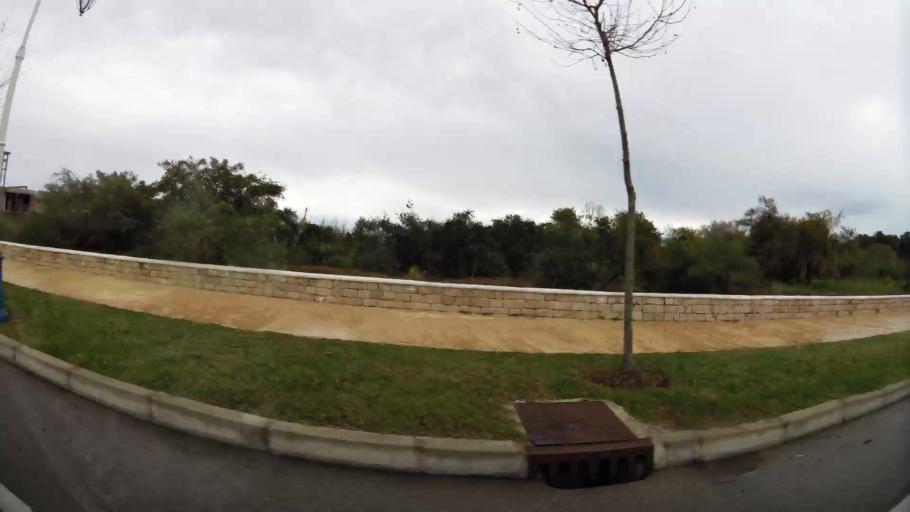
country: MA
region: Tanger-Tetouan
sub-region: Tetouan
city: Martil
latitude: 35.6590
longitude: -5.2923
